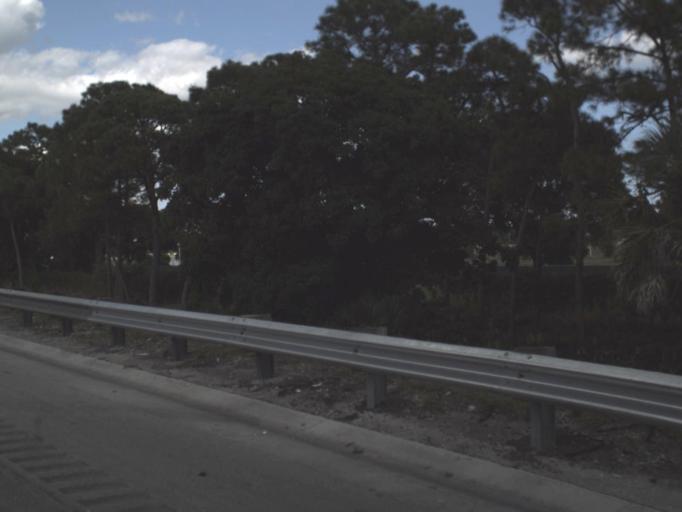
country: US
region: Florida
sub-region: Broward County
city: Davie
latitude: 26.0371
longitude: -80.2136
